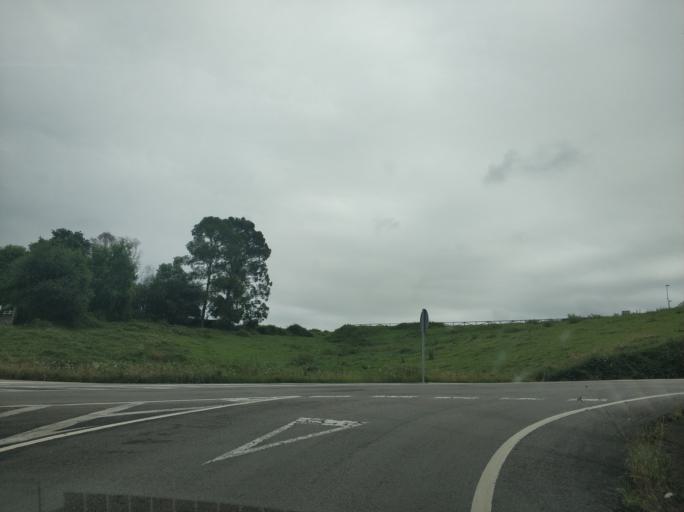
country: ES
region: Asturias
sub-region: Province of Asturias
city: Cudillero
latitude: 43.5583
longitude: -6.2858
